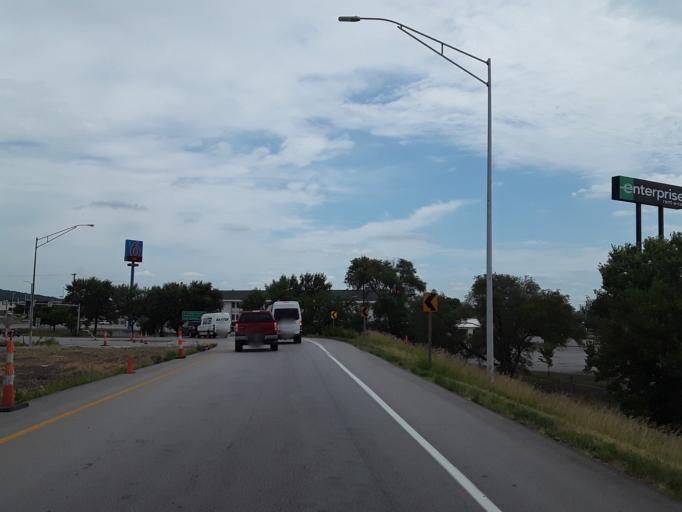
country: US
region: Iowa
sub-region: Pottawattamie County
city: Council Bluffs
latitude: 41.2311
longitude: -95.8540
